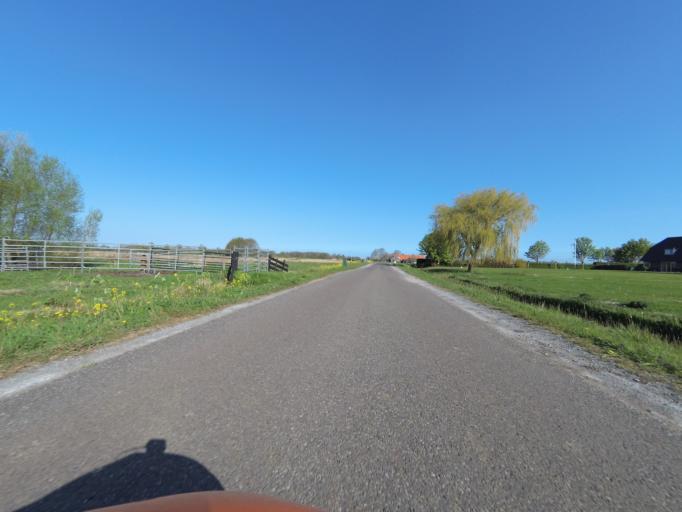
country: NL
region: North Holland
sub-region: Gemeente Naarden
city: Naarden
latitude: 52.3039
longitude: 5.1259
